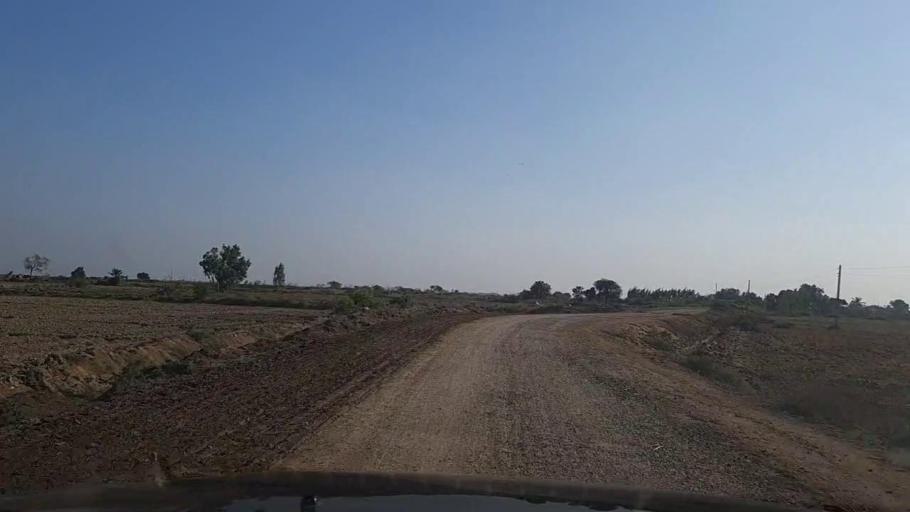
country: PK
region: Sindh
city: Gharo
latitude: 24.7075
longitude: 67.7043
